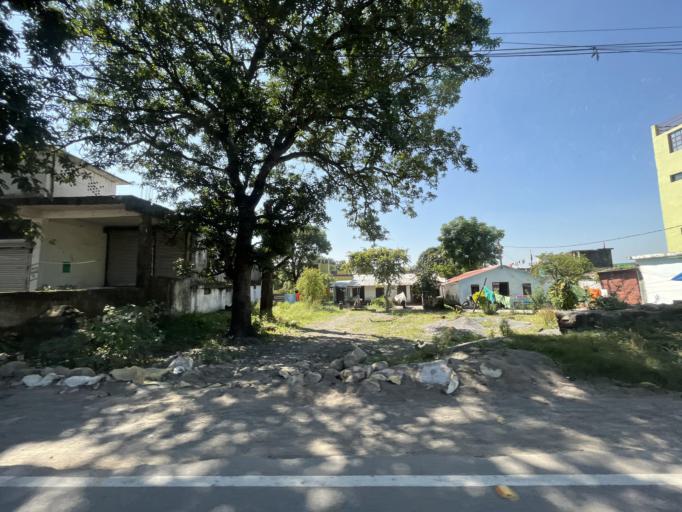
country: IN
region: Uttarakhand
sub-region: Naini Tal
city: Kaladhungi
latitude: 29.2868
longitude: 79.3455
